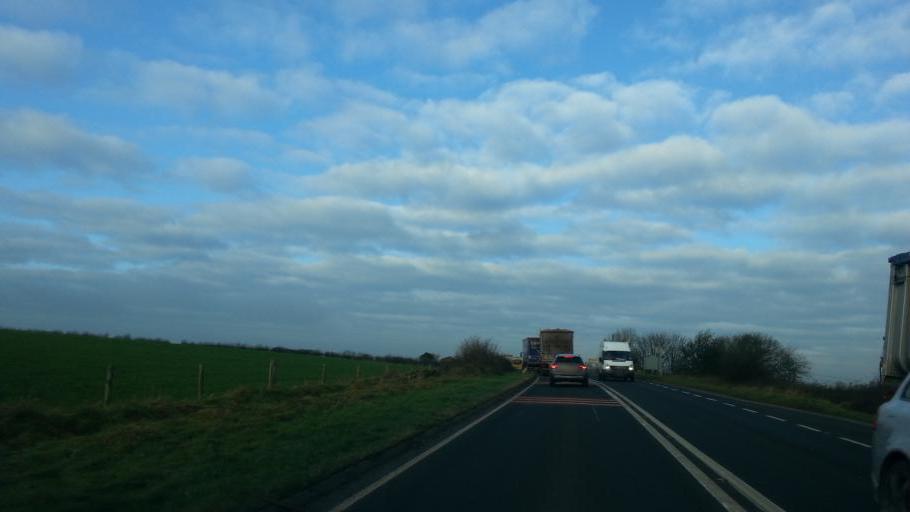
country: GB
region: England
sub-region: South Gloucestershire
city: Cold Ashton
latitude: 51.4379
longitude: -2.3680
